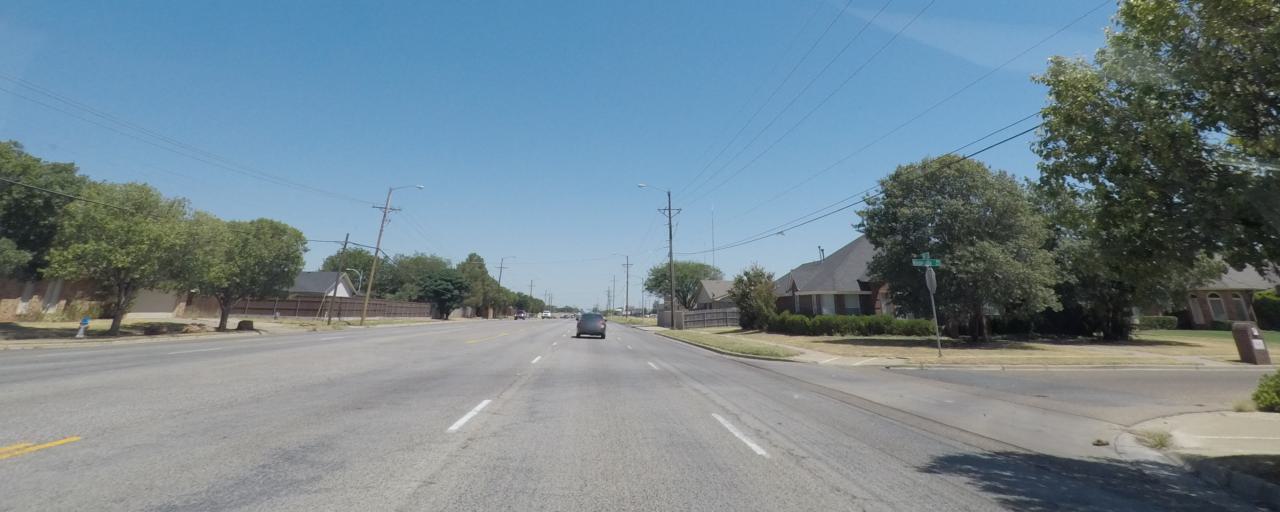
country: US
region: Texas
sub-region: Lubbock County
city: Lubbock
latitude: 33.5052
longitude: -101.8926
